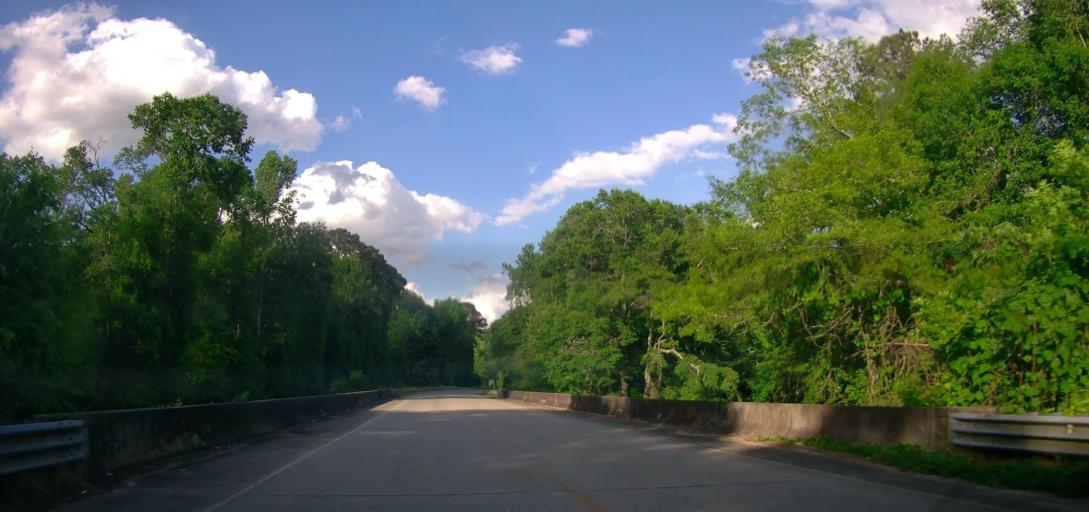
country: US
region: Georgia
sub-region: Peach County
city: Byron
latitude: 32.7195
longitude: -83.7761
